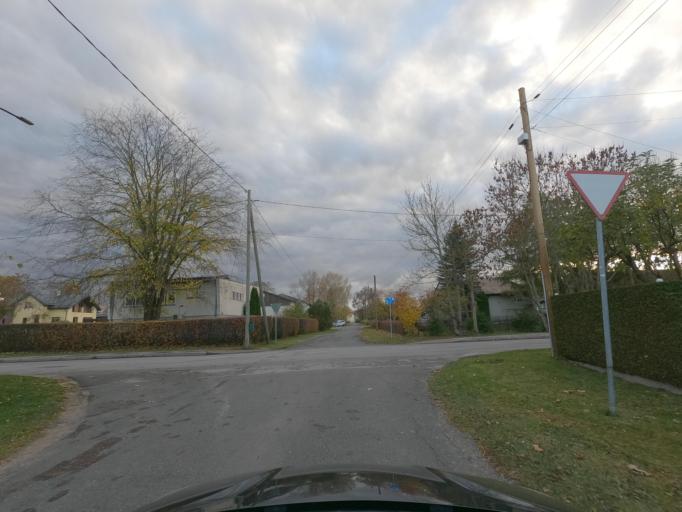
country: EE
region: Harju
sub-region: Saue linn
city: Saue
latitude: 59.3190
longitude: 24.5448
